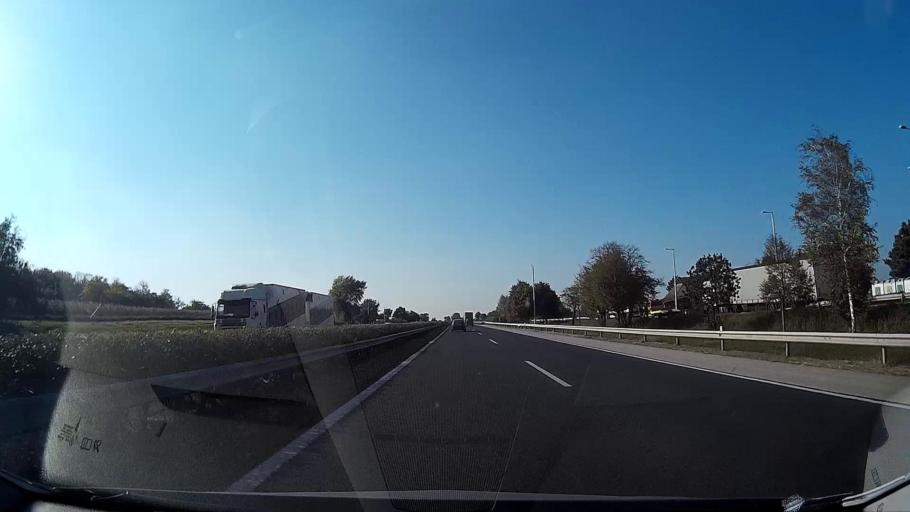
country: HU
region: Komarom-Esztergom
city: Kocs
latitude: 47.6343
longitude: 18.2442
